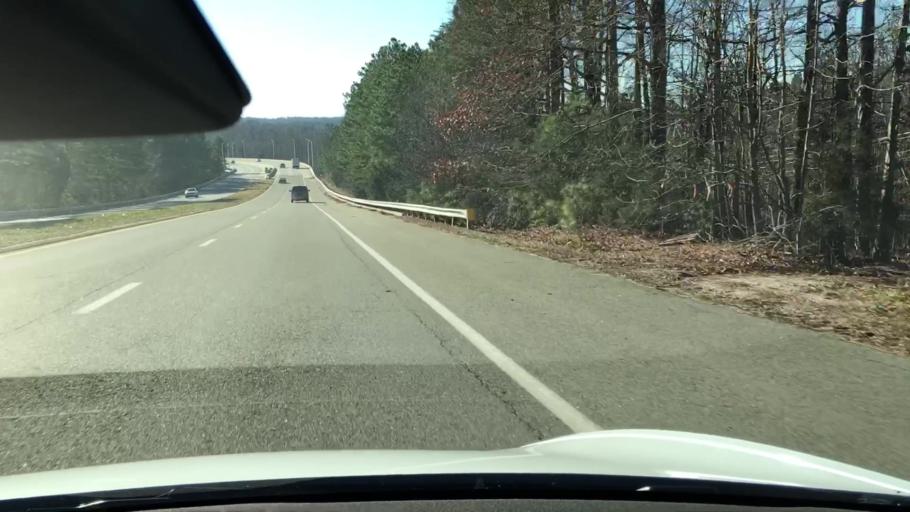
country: US
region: Virginia
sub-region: Henrico County
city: Tuckahoe
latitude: 37.5687
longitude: -77.5776
